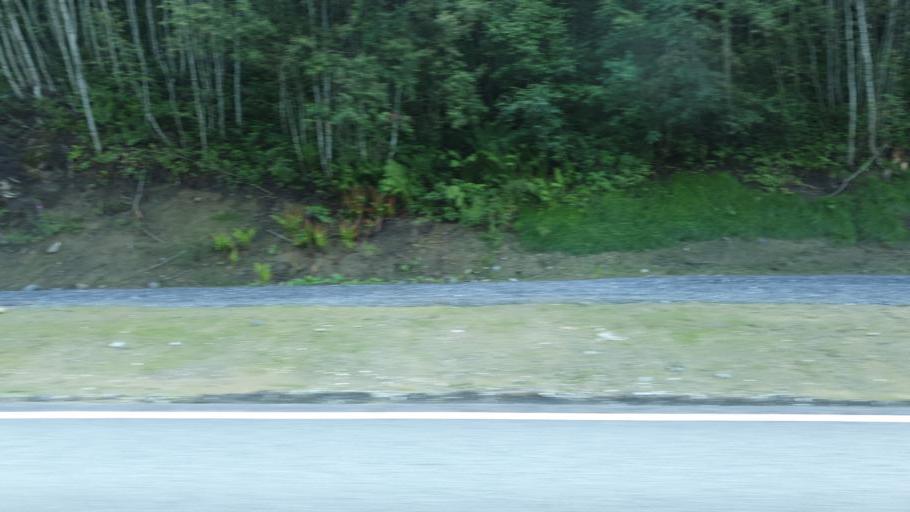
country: NO
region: Sor-Trondelag
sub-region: Midtre Gauldal
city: Storen
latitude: 62.9817
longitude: 10.2354
